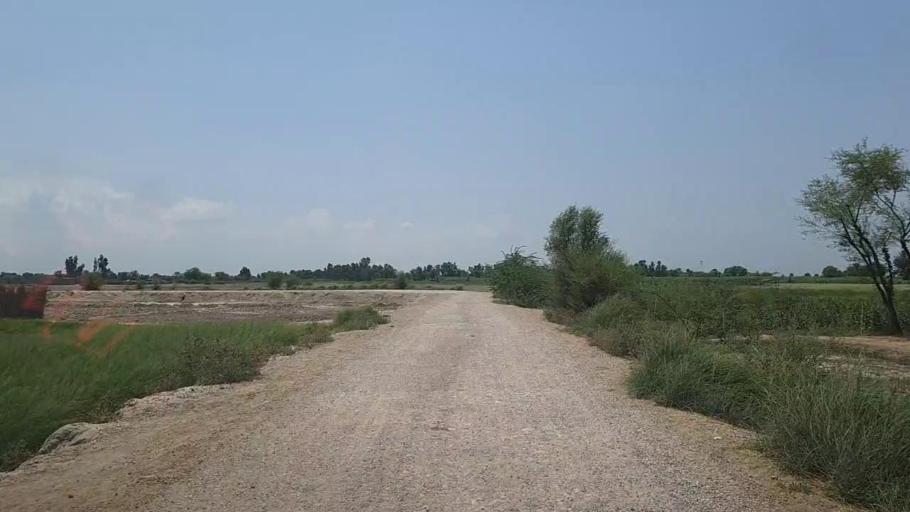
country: PK
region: Sindh
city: Ubauro
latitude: 28.1557
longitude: 69.7643
